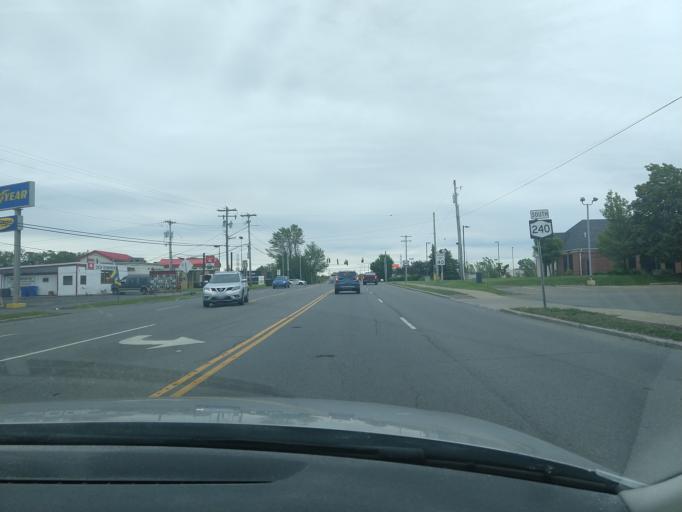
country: US
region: New York
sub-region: Erie County
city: West Seneca
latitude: 42.8355
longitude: -78.7881
